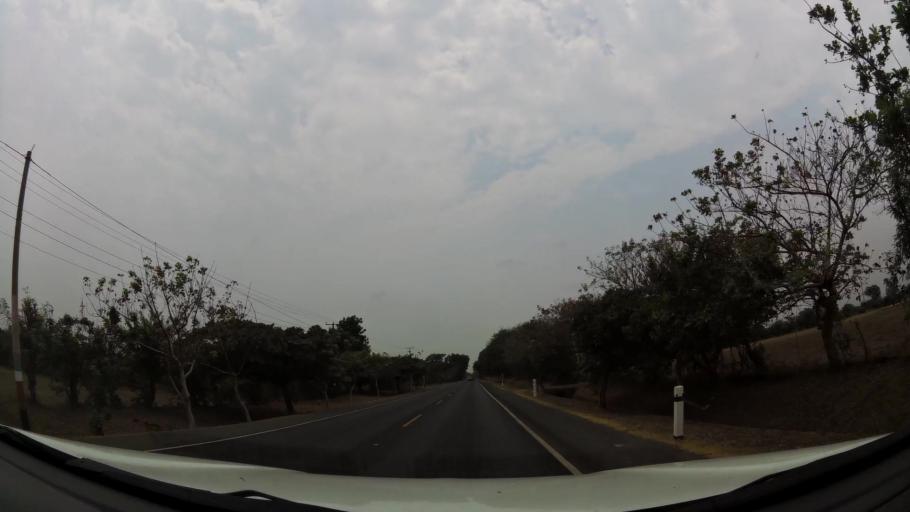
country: NI
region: Chinandega
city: Chichigalpa
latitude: 12.5938
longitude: -87.0285
